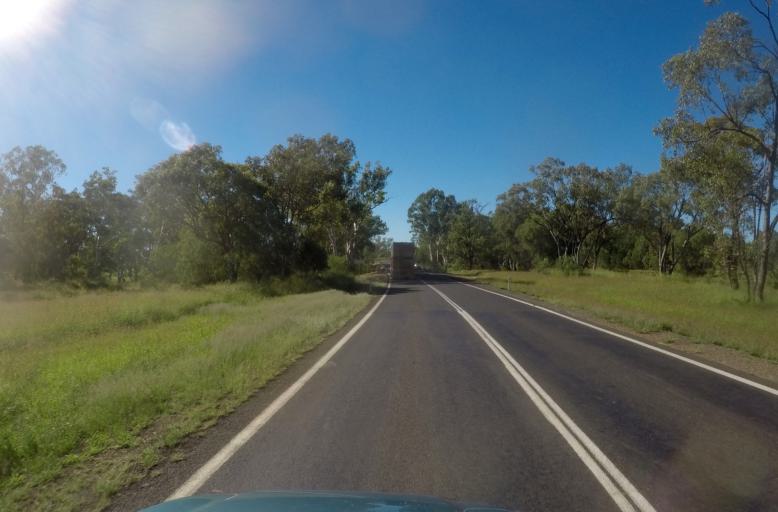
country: AU
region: Queensland
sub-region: Maranoa
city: Roma
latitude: -26.4338
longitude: 148.7942
